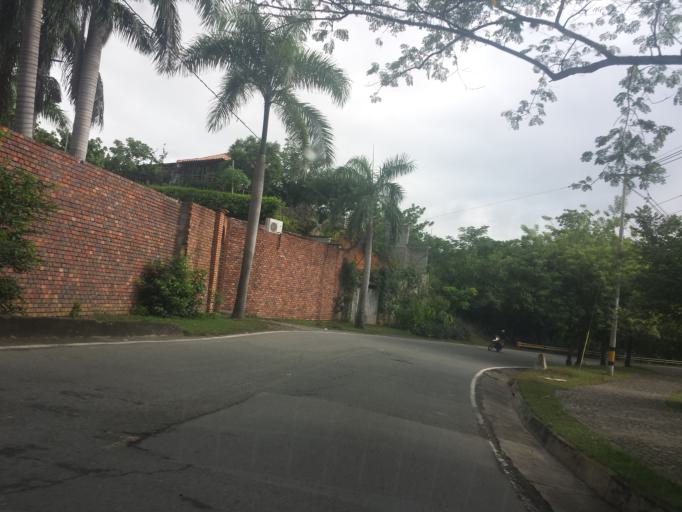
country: CO
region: Antioquia
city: Antioquia
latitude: 6.5507
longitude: -75.8225
